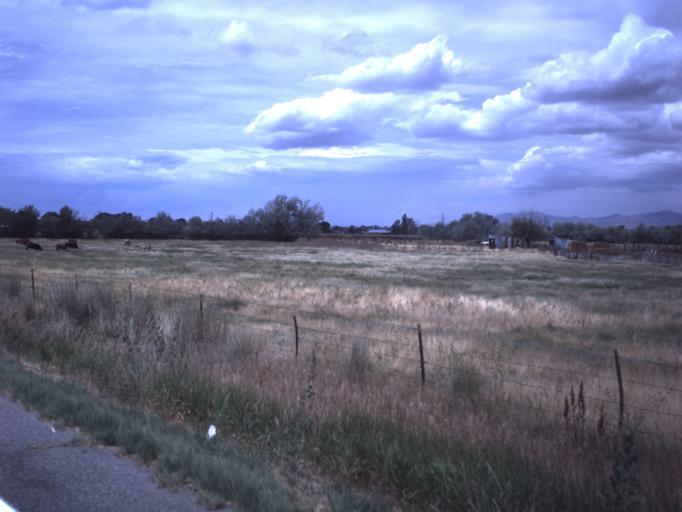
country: US
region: Utah
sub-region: Weber County
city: West Haven
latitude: 41.2030
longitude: -112.0330
